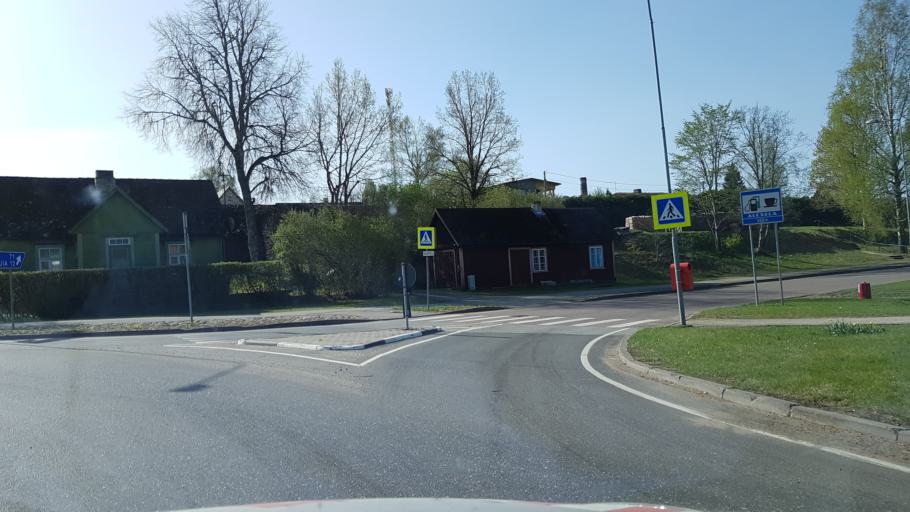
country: EE
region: Viljandimaa
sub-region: Abja vald
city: Abja-Paluoja
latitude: 58.1259
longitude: 25.3591
